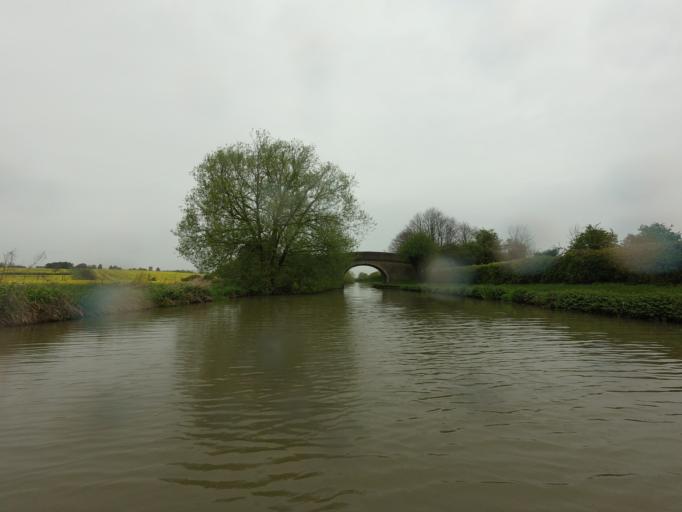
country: GB
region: England
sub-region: Northamptonshire
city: Hartwell
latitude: 52.1087
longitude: -0.8865
